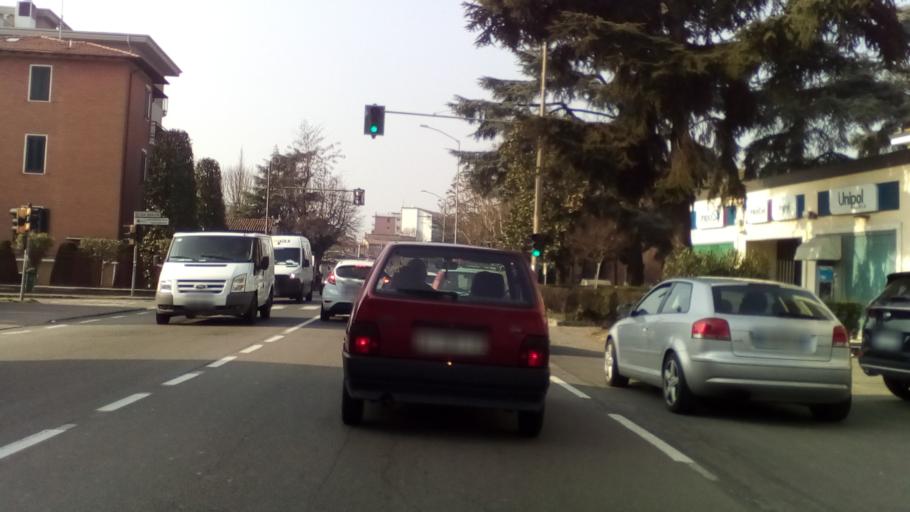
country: IT
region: Emilia-Romagna
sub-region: Provincia di Modena
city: Modena
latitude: 44.6331
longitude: 10.9383
